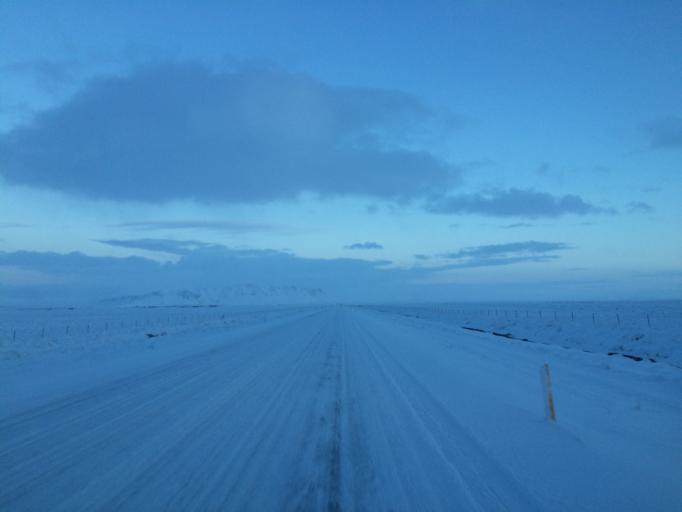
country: IS
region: South
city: Selfoss
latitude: 63.8711
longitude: -21.0981
